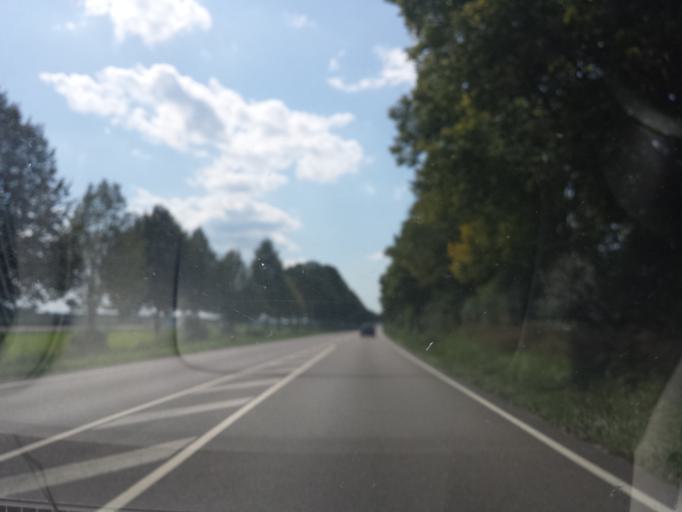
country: DE
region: Bavaria
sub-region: Upper Bavaria
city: Ernsgaden
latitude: 48.7271
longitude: 11.5497
